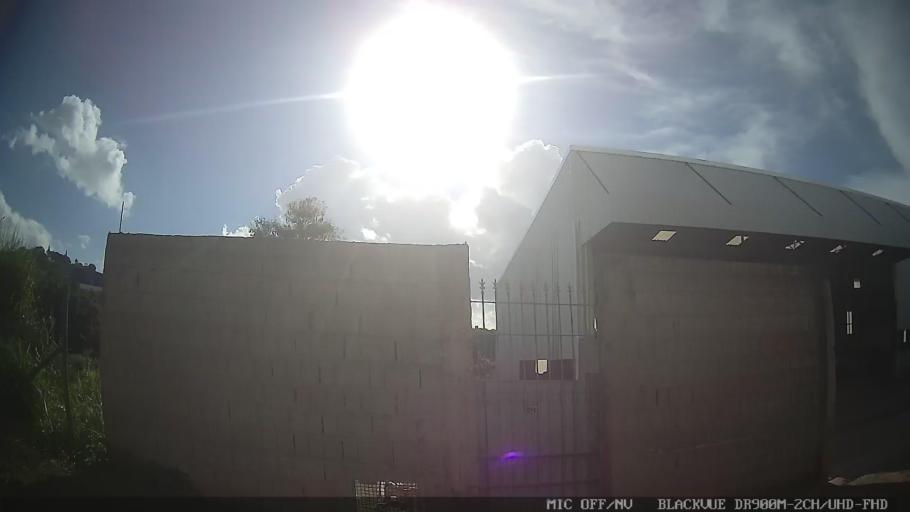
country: BR
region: Sao Paulo
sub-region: Bom Jesus Dos Perdoes
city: Bom Jesus dos Perdoes
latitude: -23.1229
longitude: -46.4831
